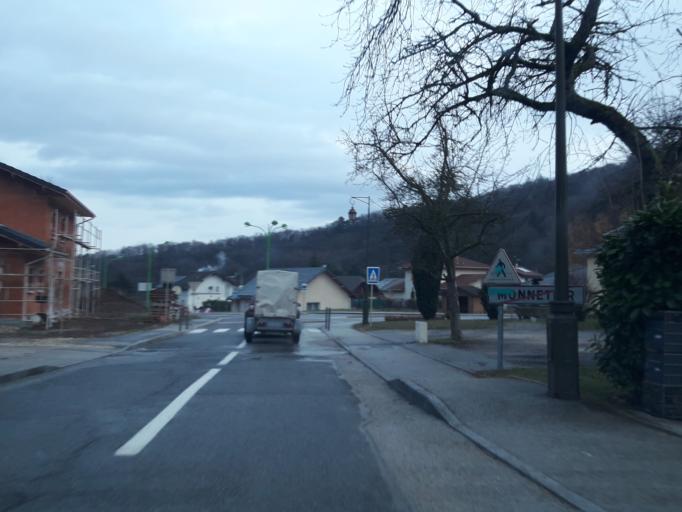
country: FR
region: Rhone-Alpes
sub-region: Departement de la Haute-Savoie
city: Monnetier-Mornex
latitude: 46.1594
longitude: 6.2137
